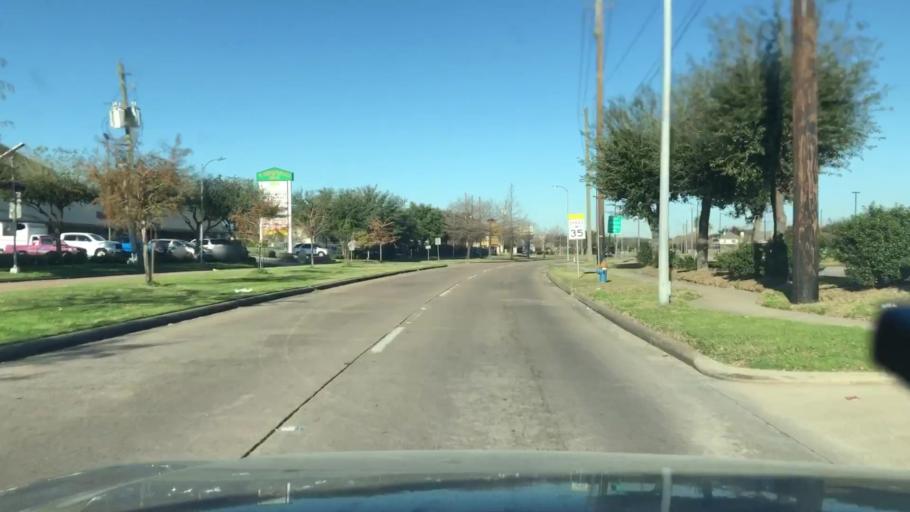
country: US
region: Texas
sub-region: Fort Bend County
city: Missouri City
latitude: 29.6422
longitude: -95.5284
